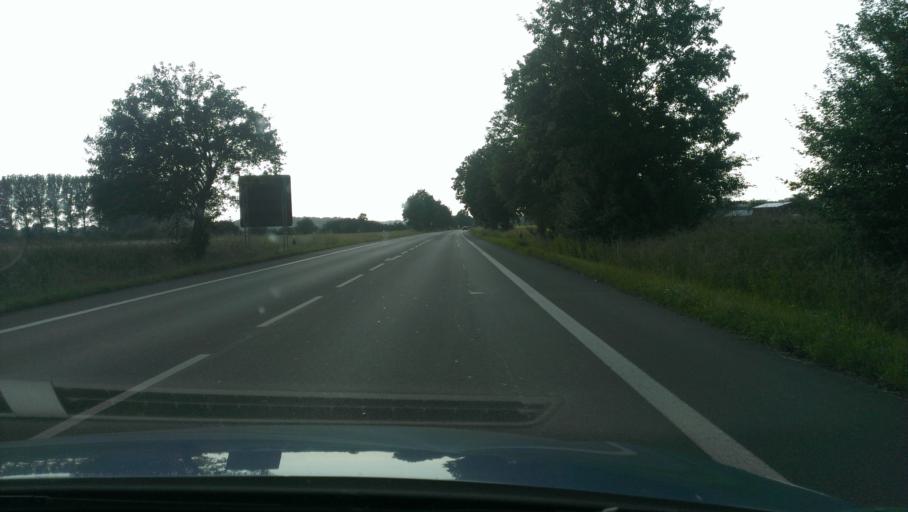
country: DE
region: North Rhine-Westphalia
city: Ahlen
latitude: 51.8195
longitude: 7.9151
